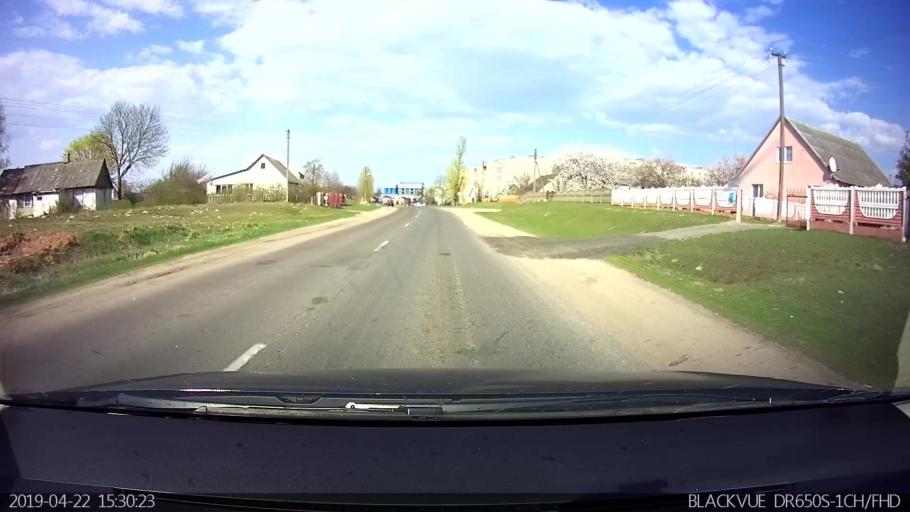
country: BY
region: Brest
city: Vysokaye
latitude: 52.3977
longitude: 23.3785
